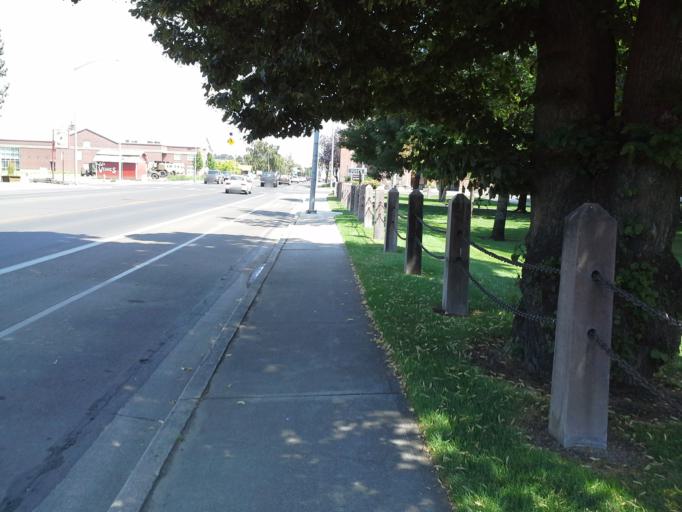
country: US
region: Oregon
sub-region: Baker County
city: Baker City
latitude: 44.7816
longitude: -117.8267
